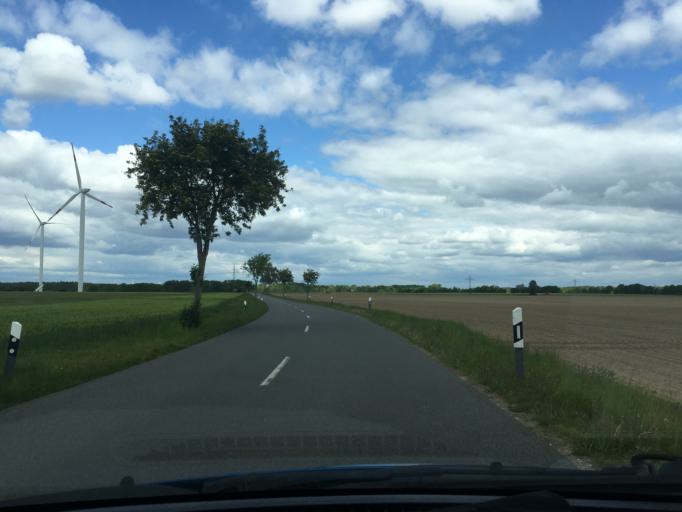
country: DE
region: Lower Saxony
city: Suderburg
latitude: 52.9120
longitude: 10.4401
